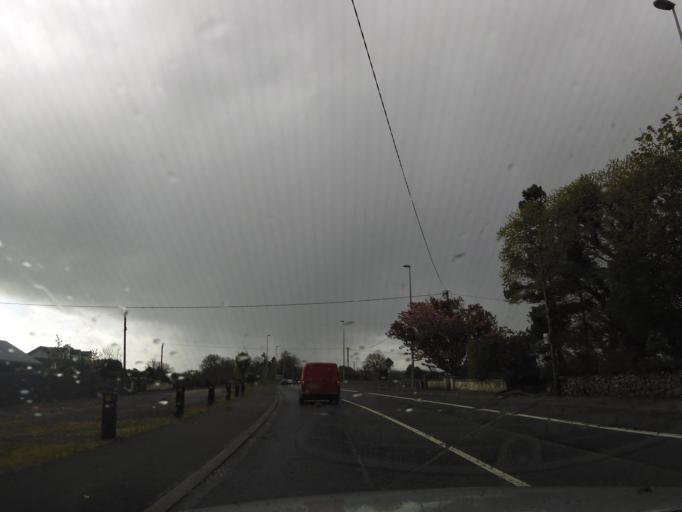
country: IE
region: Connaught
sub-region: County Galway
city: Claregalway
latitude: 53.3313
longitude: -8.9623
